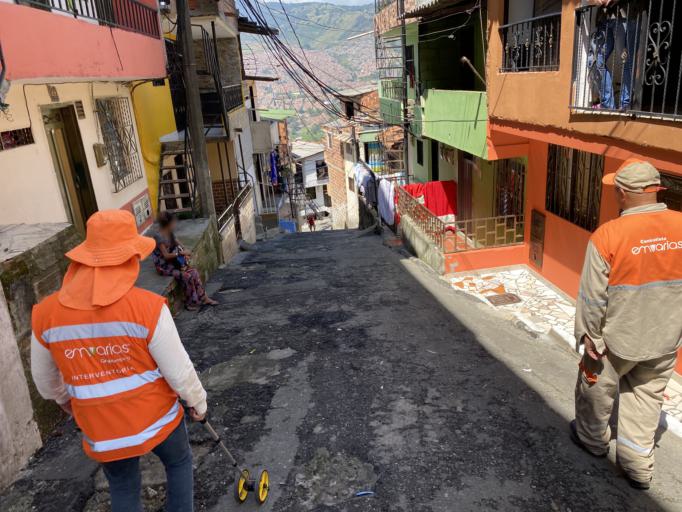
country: CO
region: Antioquia
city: Bello
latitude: 6.3003
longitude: -75.5459
